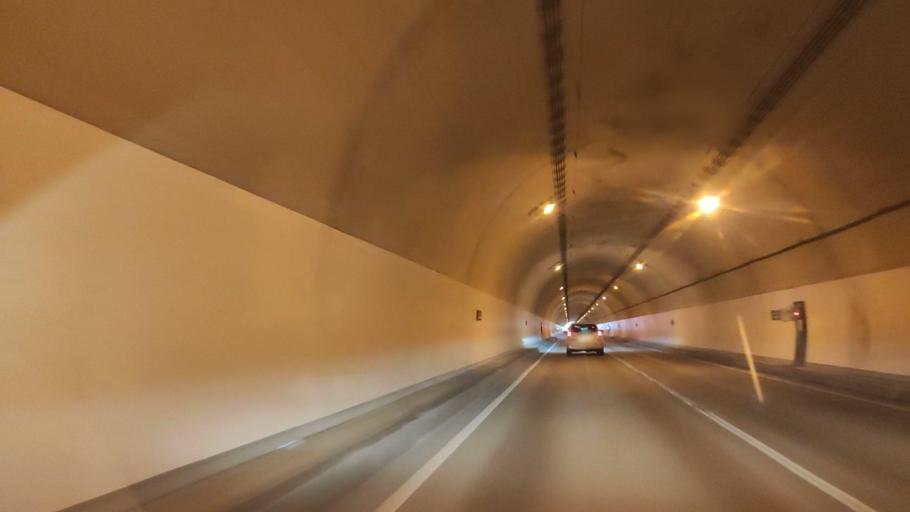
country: JP
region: Hokkaido
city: Ishikari
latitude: 43.4761
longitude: 141.3952
